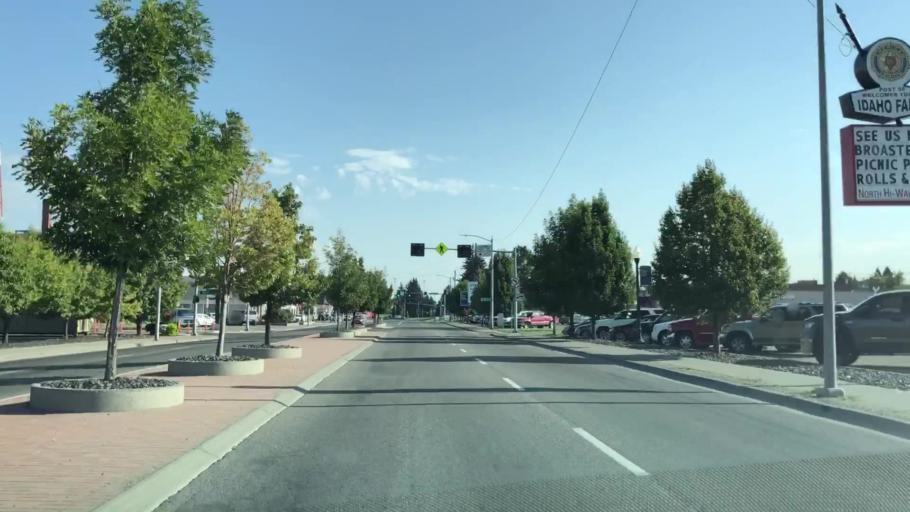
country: US
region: Idaho
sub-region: Bonneville County
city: Idaho Falls
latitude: 43.4920
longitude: -112.0382
